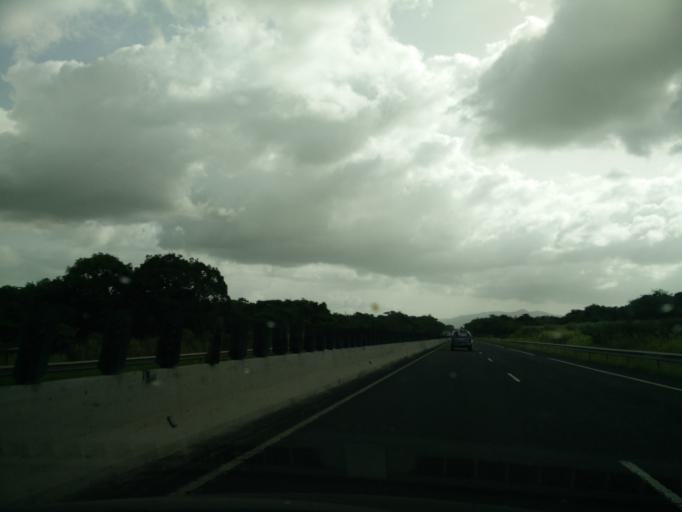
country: GP
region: Guadeloupe
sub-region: Guadeloupe
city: Baie-Mahault
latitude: 16.2668
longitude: -61.5616
